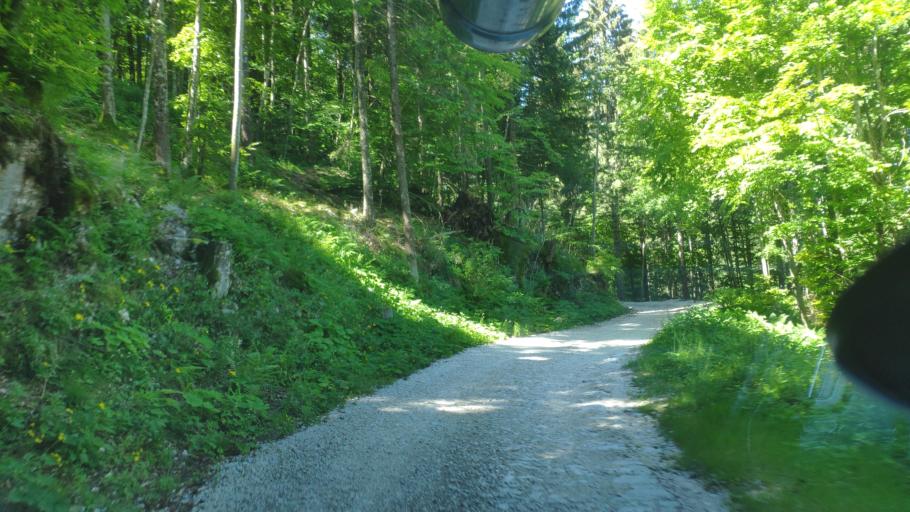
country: IT
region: Veneto
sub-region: Provincia di Vicenza
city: Cogollo del Cengio
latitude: 45.8216
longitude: 11.4493
